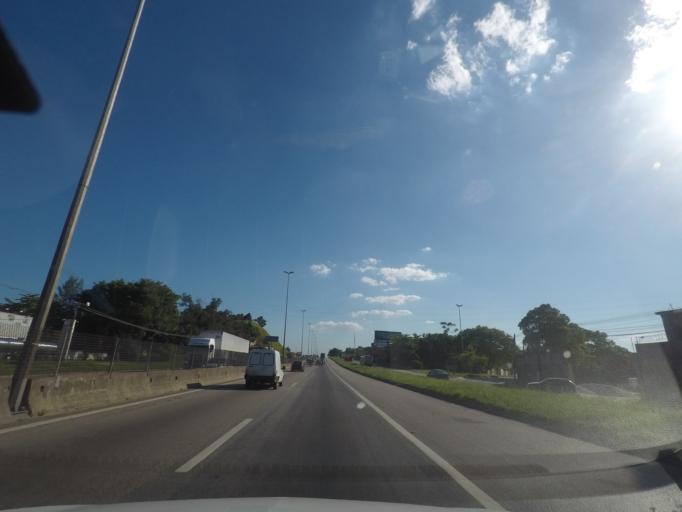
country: BR
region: Rio de Janeiro
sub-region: Duque De Caxias
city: Duque de Caxias
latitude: -22.6953
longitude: -43.2885
